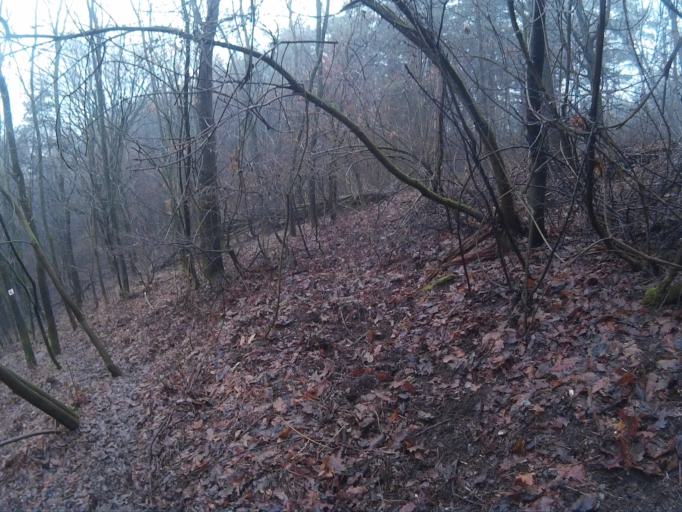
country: HU
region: Nograd
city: Somoskoujfalu
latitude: 48.1378
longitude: 19.8499
